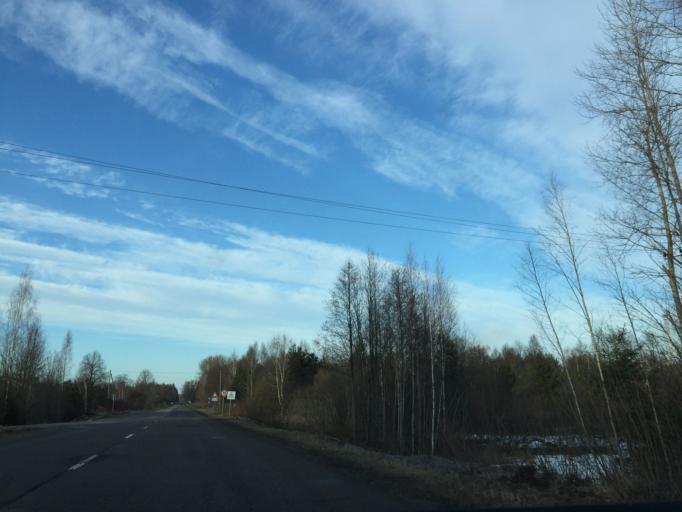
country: LV
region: Kekava
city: Balozi
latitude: 56.7311
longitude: 24.1098
